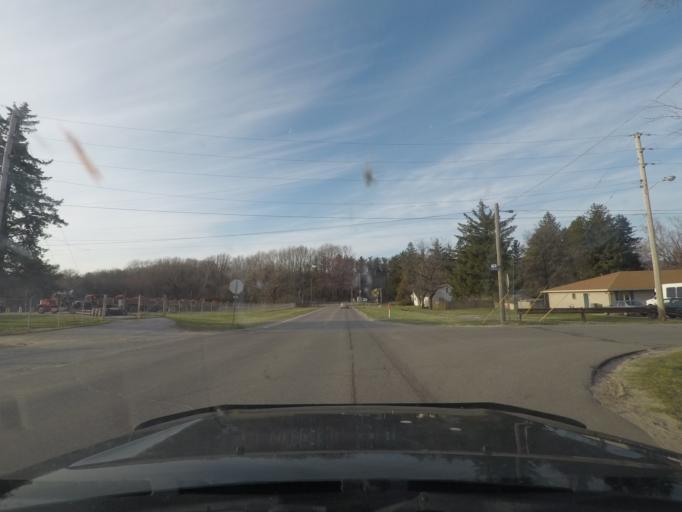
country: US
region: Indiana
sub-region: LaPorte County
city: LaPorte
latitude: 41.6031
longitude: -86.7476
